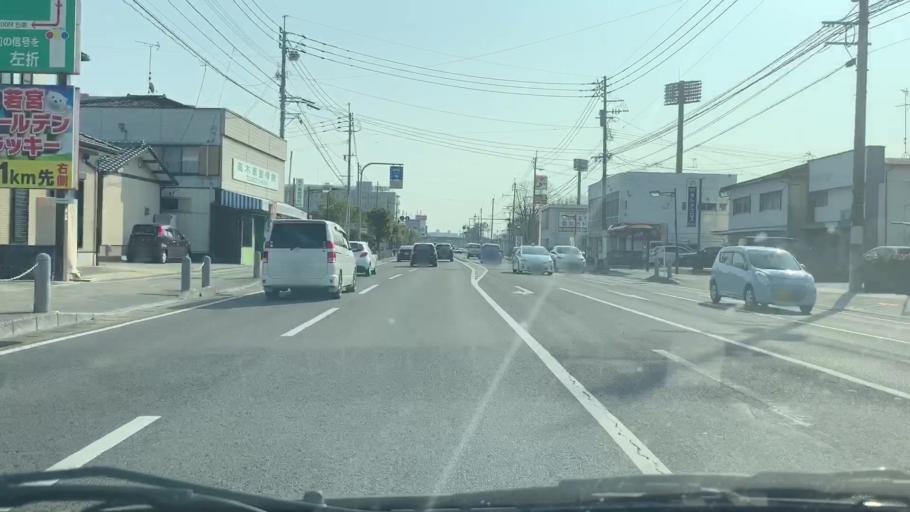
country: JP
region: Saga Prefecture
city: Saga-shi
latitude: 33.2793
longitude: 130.2924
